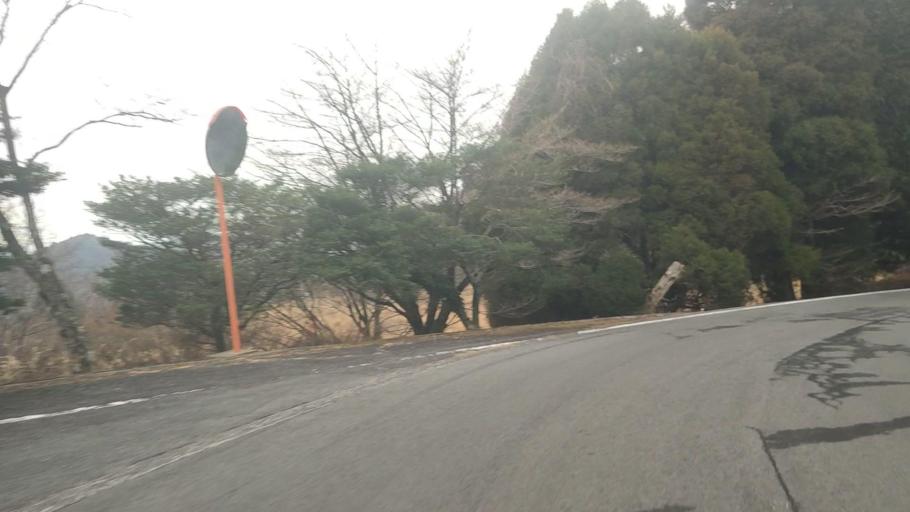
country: JP
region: Nagasaki
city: Shimabara
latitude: 32.7497
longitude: 130.2754
